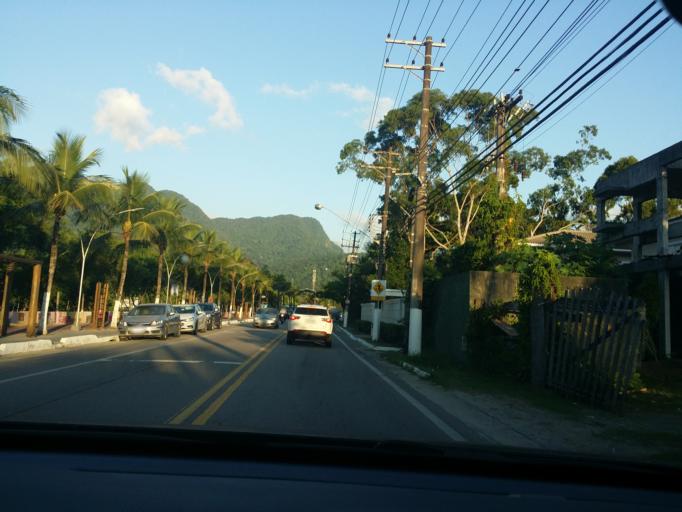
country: BR
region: Sao Paulo
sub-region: Sao Sebastiao
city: Sao Sebastiao
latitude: -23.7902
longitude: -45.5687
